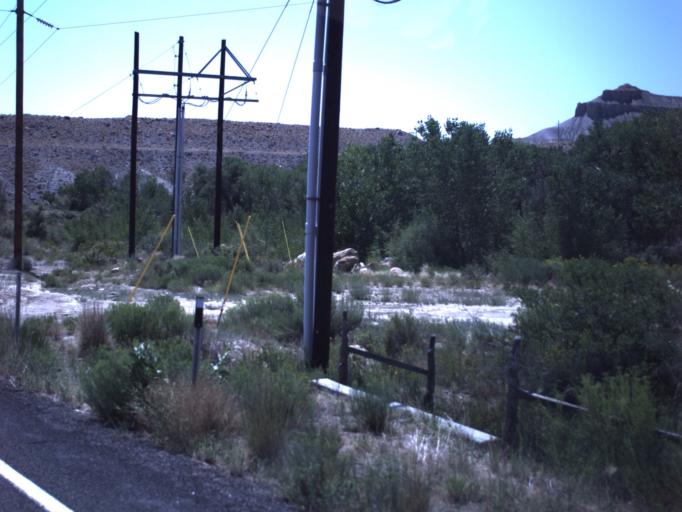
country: US
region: Utah
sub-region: Emery County
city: Orangeville
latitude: 39.2498
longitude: -111.0952
